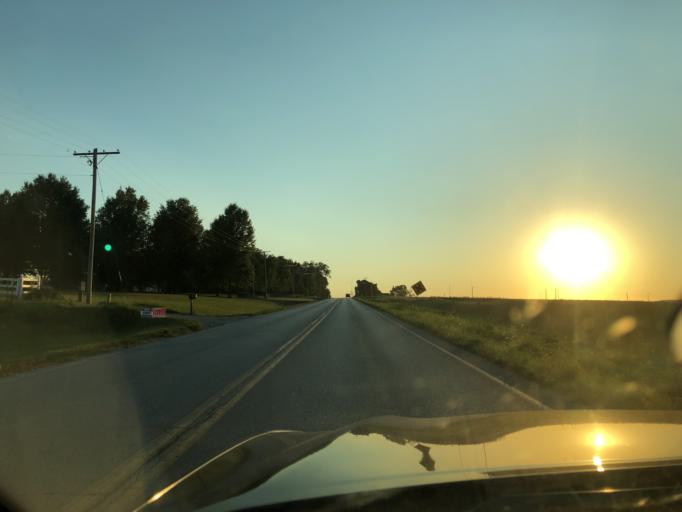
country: US
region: Kansas
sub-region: Leavenworth County
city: Lansing
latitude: 39.2668
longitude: -94.9426
